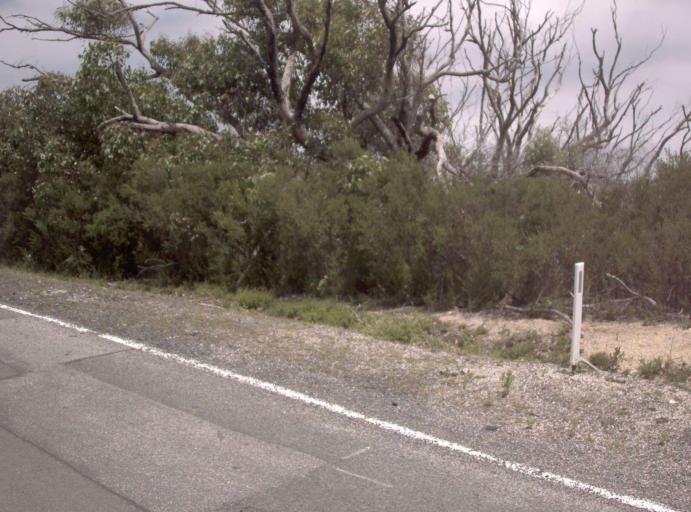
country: AU
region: Victoria
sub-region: Latrobe
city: Morwell
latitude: -39.0120
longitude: 146.2983
